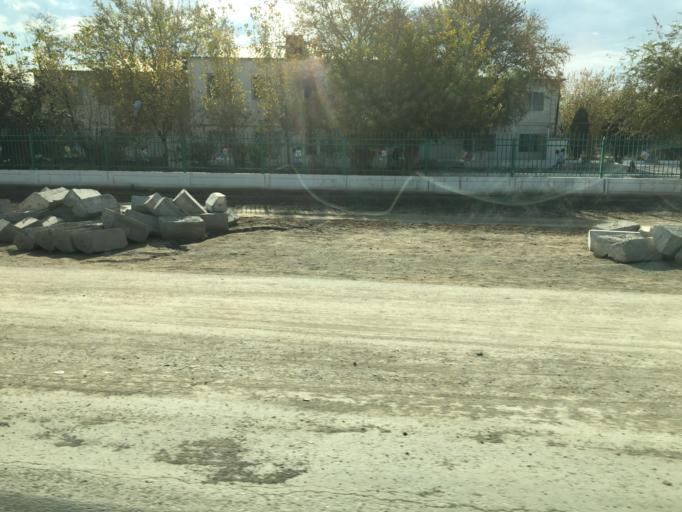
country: TM
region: Ahal
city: Tejen
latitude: 37.3718
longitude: 60.5080
